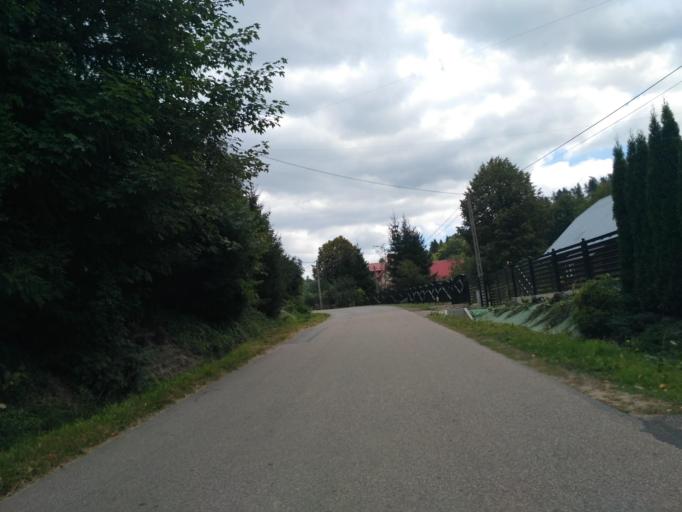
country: PL
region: Subcarpathian Voivodeship
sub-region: Powiat rzeszowski
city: Dynow
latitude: 49.7726
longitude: 22.2468
